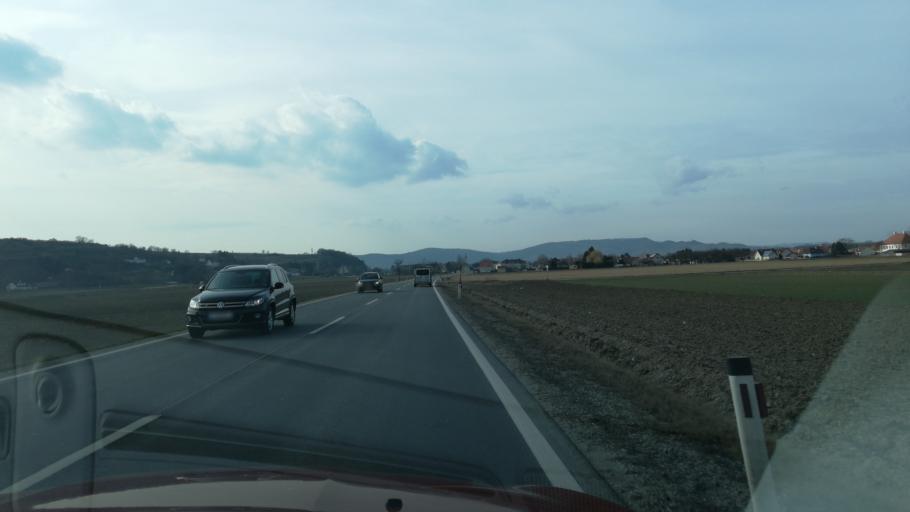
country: AT
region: Lower Austria
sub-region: Politischer Bezirk Sankt Polten
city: Traismauer
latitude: 48.3479
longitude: 15.7661
